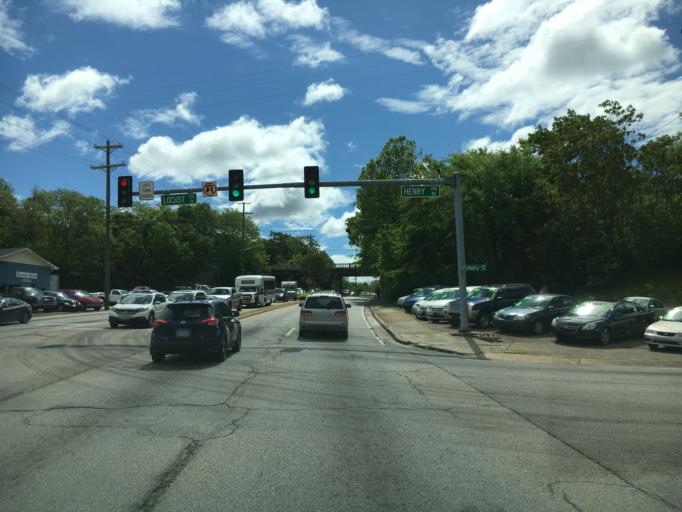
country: US
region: Virginia
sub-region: City of Danville
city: Danville
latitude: 36.5971
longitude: -79.3958
